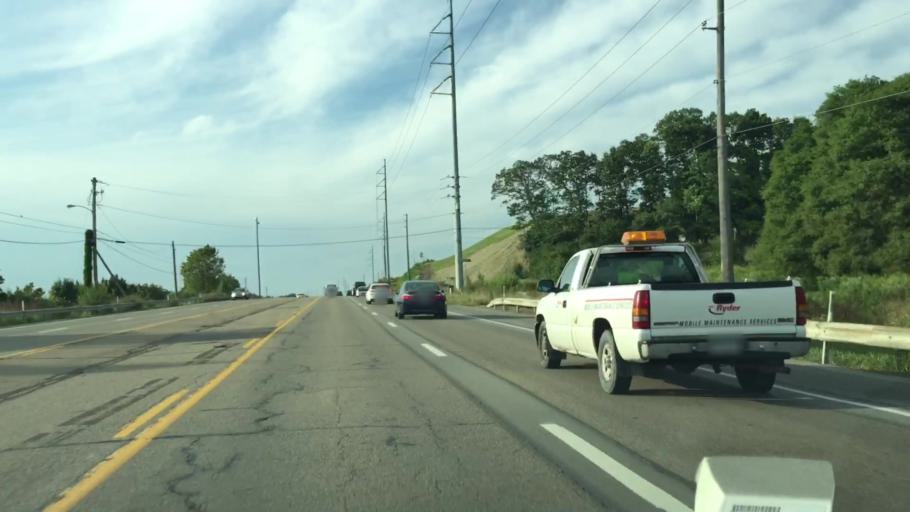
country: US
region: Pennsylvania
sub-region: Butler County
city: Fox Run
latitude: 40.7264
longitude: -80.1073
